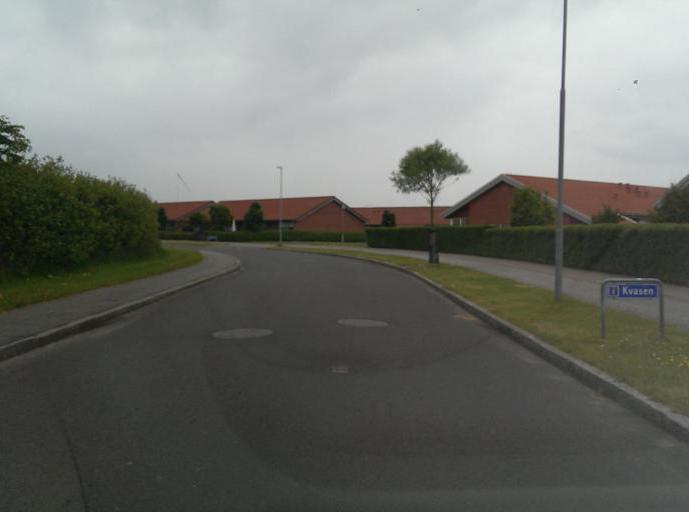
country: DK
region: South Denmark
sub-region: Fano Kommune
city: Nordby
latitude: 55.5343
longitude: 8.3570
